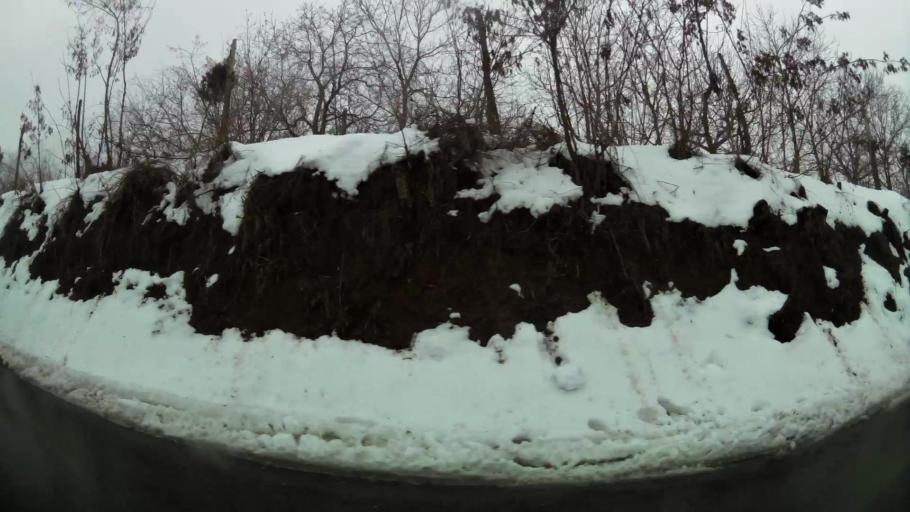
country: RS
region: Central Serbia
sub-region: Belgrade
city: Zvezdara
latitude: 44.7488
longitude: 20.5096
